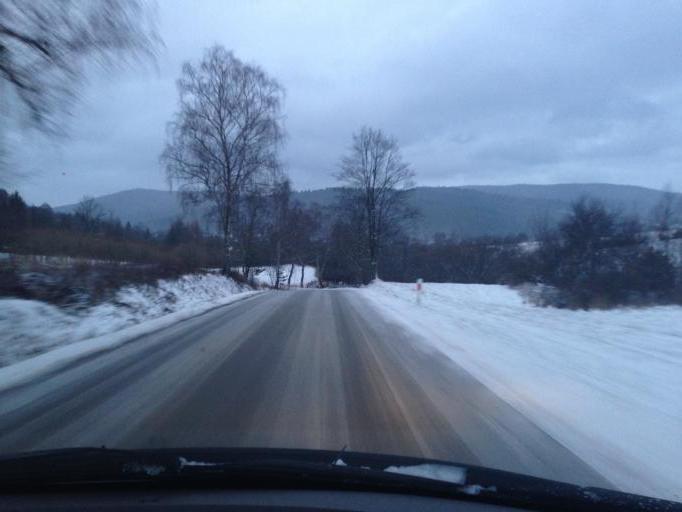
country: PL
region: Subcarpathian Voivodeship
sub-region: Powiat jasielski
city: Krempna
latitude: 49.5201
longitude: 21.5025
